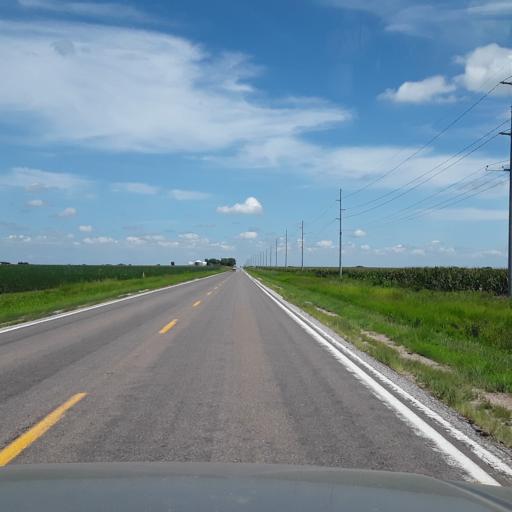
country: US
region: Nebraska
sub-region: York County
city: York
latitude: 40.9315
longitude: -97.4063
